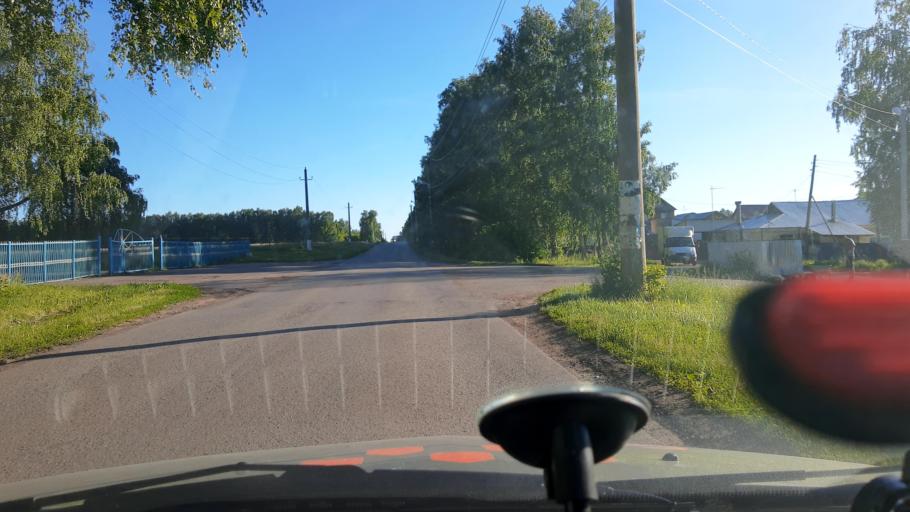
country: RU
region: Bashkortostan
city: Chishmy
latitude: 54.5977
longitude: 55.3713
